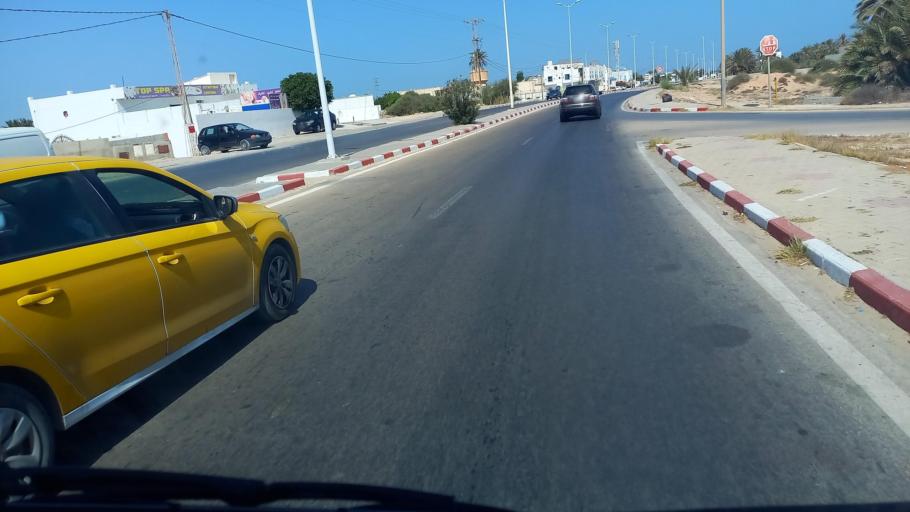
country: TN
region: Madanin
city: Midoun
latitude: 33.8626
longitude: 10.9639
